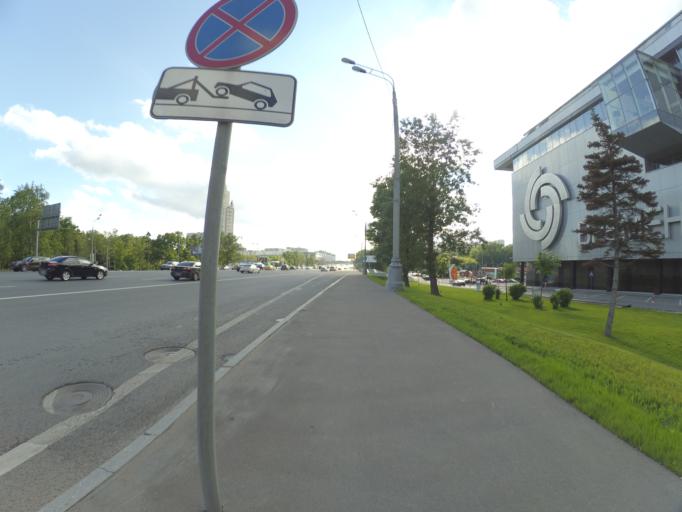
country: RU
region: Moskovskaya
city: Fili
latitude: 55.7312
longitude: 37.4869
